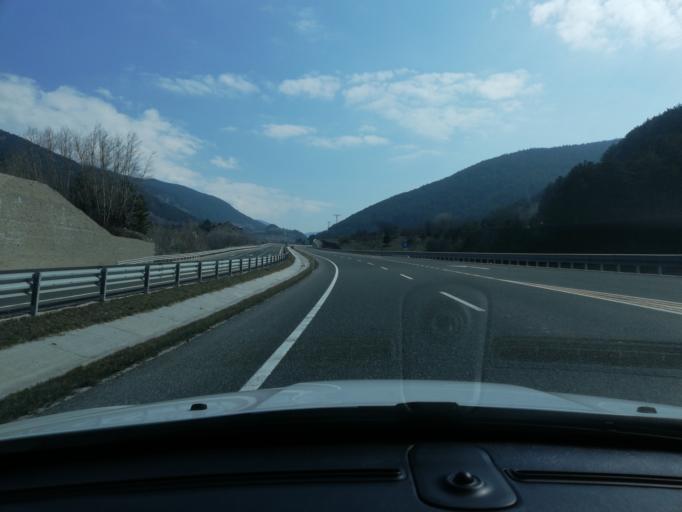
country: TR
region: Cankiri
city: Ilgaz
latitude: 41.0268
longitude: 33.7239
